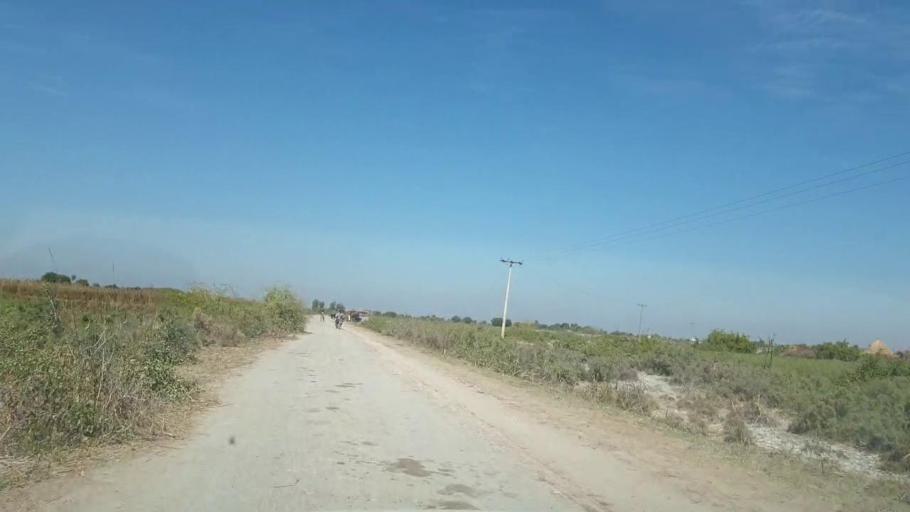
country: PK
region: Sindh
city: Pithoro
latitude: 25.6240
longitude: 69.2154
